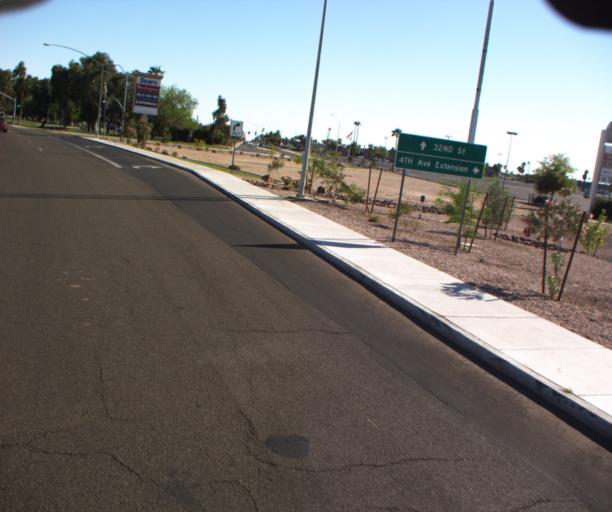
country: US
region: Arizona
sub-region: Yuma County
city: Yuma
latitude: 32.6723
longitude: -114.6244
